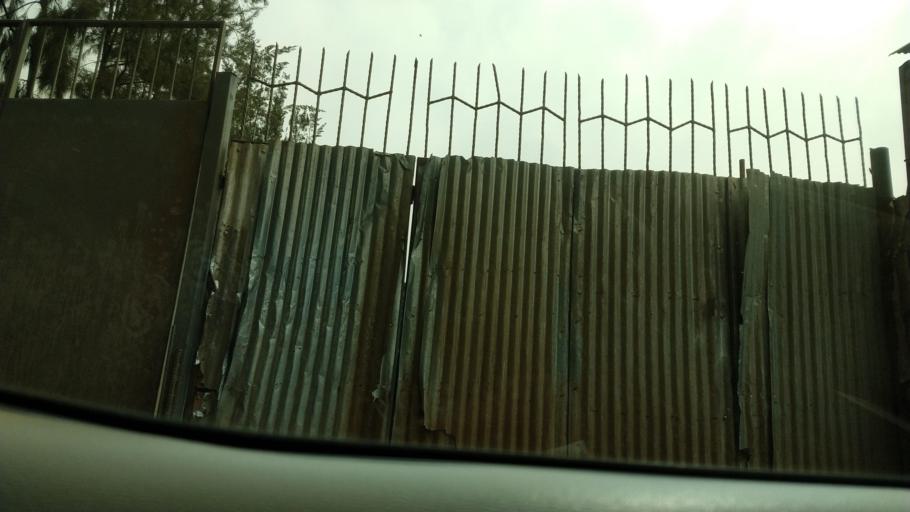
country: KE
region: Nairobi Area
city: Nairobi
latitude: -1.2977
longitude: 36.7793
